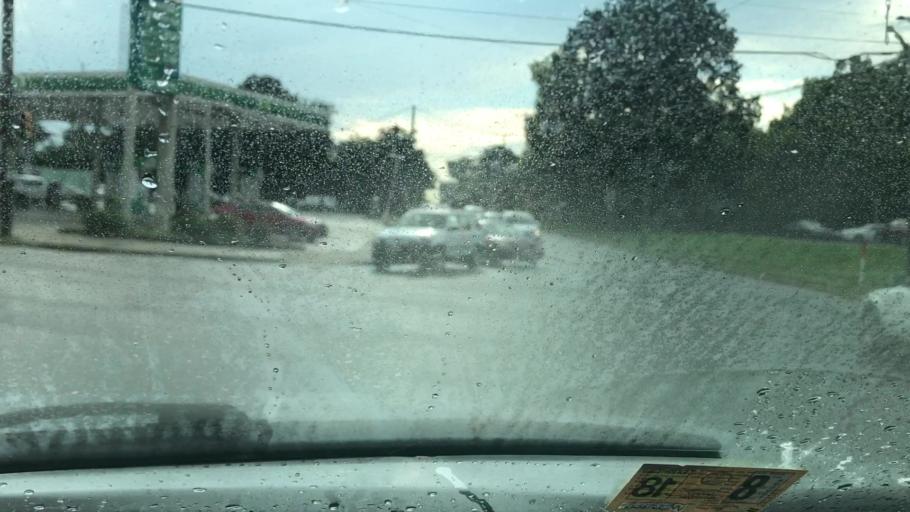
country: US
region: Virginia
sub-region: City of Richmond
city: Richmond
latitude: 37.5783
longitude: -77.4618
